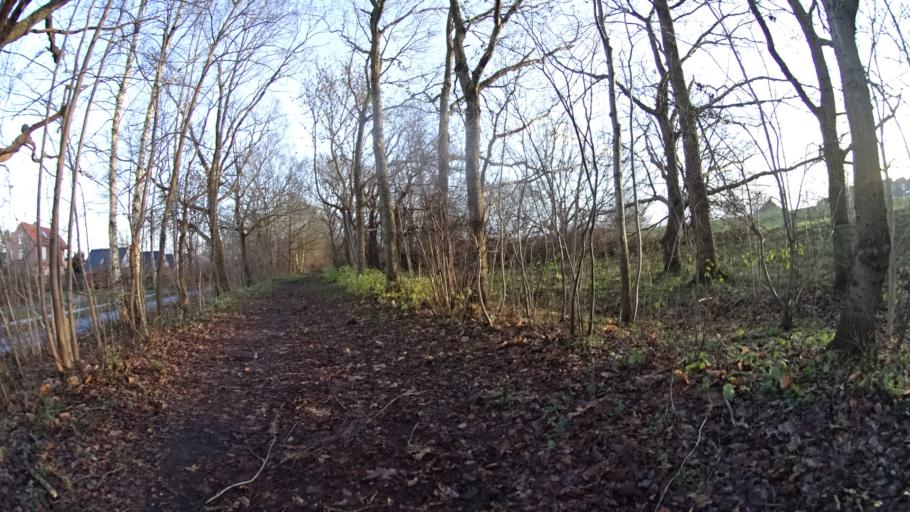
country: DK
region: Central Jutland
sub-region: Arhus Kommune
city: Stavtrup
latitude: 56.1385
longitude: 10.1226
